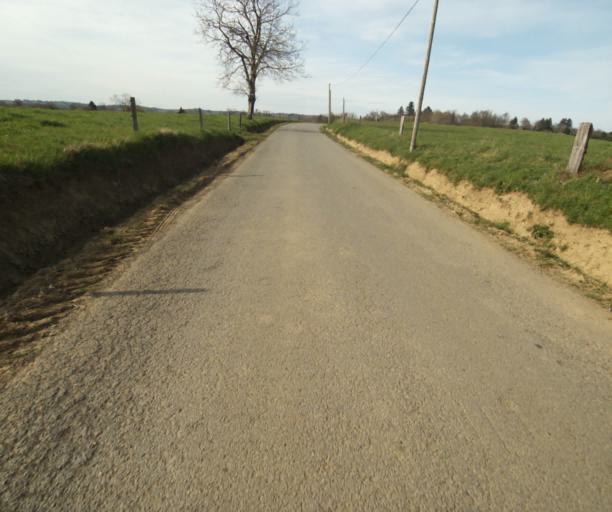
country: FR
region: Limousin
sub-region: Departement de la Correze
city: Naves
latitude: 45.3004
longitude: 1.7387
